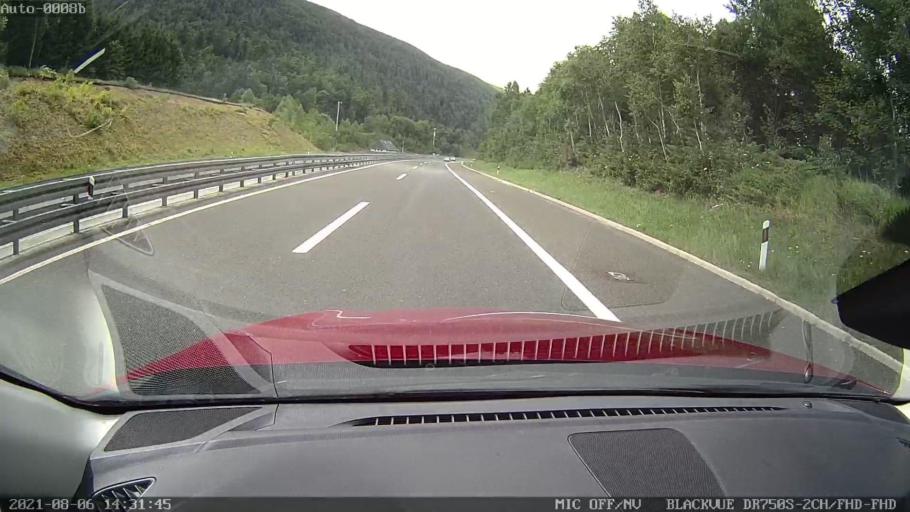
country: HR
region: Primorsko-Goranska
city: Hreljin
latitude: 45.3195
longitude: 14.6703
